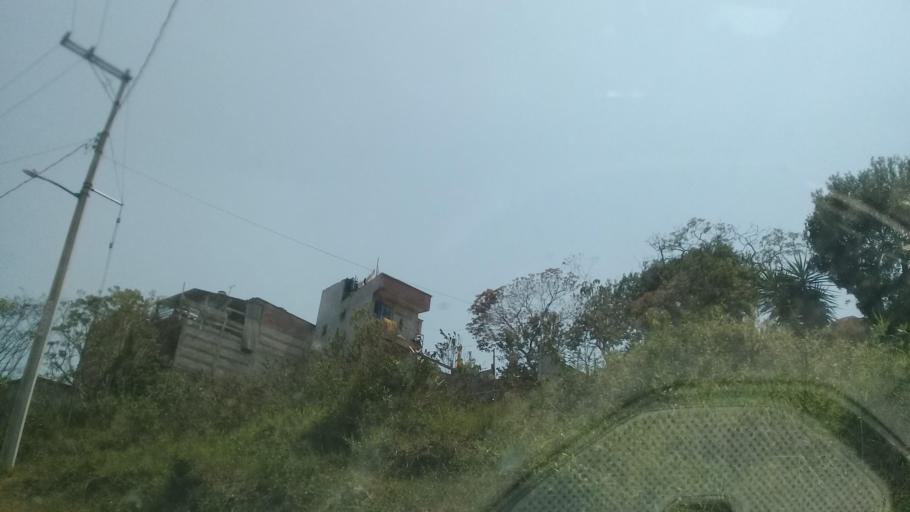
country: MX
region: Veracruz
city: El Castillo
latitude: 19.5509
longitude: -96.8584
